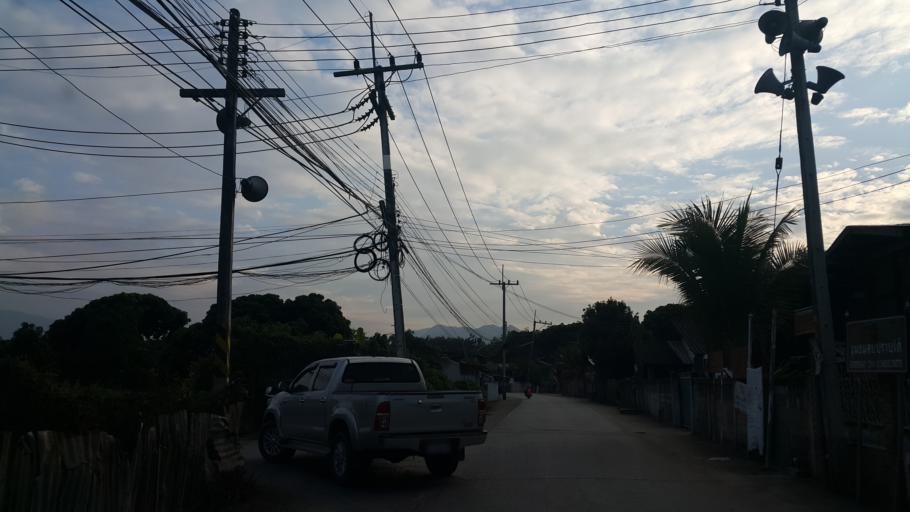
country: TH
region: Lampang
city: Sop Prap
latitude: 17.8740
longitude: 99.3325
